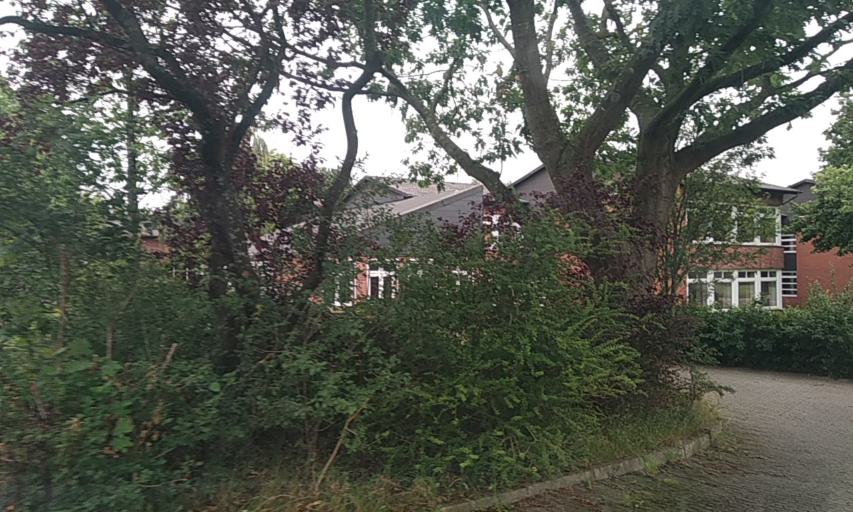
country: DE
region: Schleswig-Holstein
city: Schleswig
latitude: 54.5256
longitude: 9.5444
